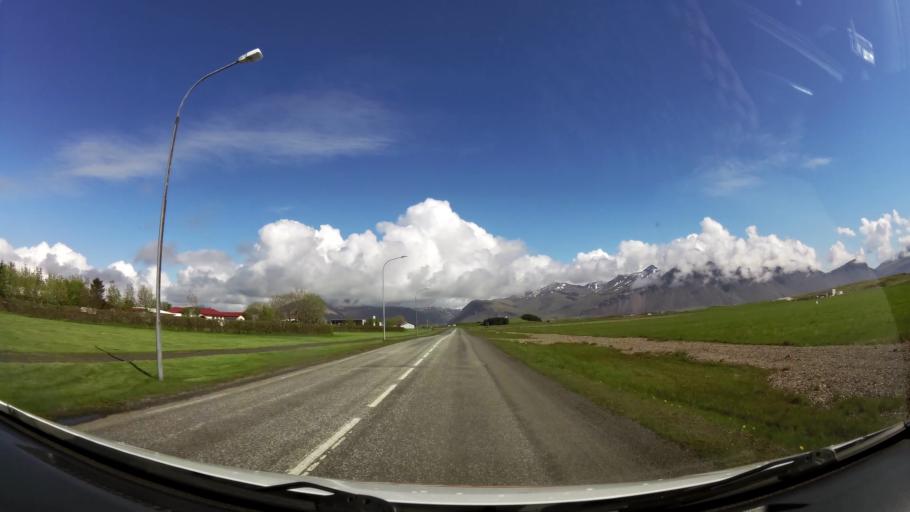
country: IS
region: East
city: Hoefn
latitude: 64.2609
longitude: -15.2035
